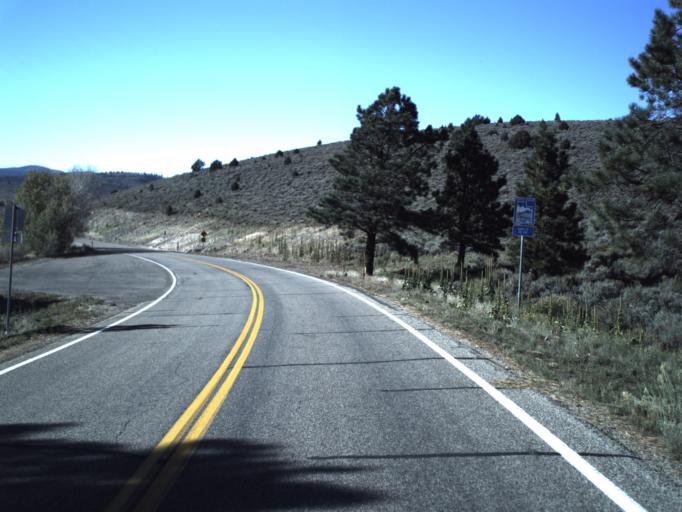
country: US
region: Utah
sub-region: Garfield County
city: Panguitch
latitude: 37.7171
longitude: -112.6230
